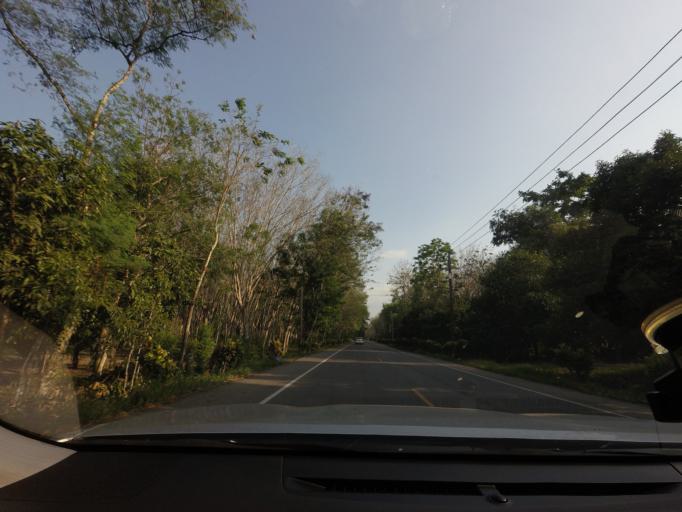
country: TH
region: Surat Thani
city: Phrasaeng
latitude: 8.5762
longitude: 99.2815
